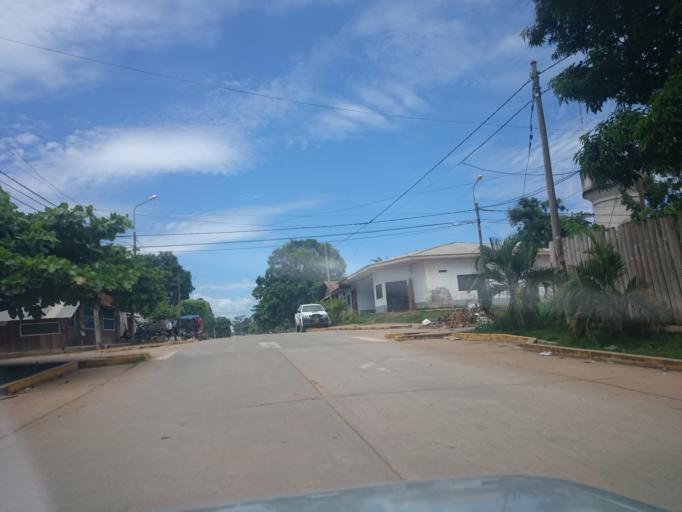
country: PE
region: Ucayali
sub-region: Provincia de Coronel Portillo
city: Puerto Callao
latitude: -8.3580
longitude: -74.5764
